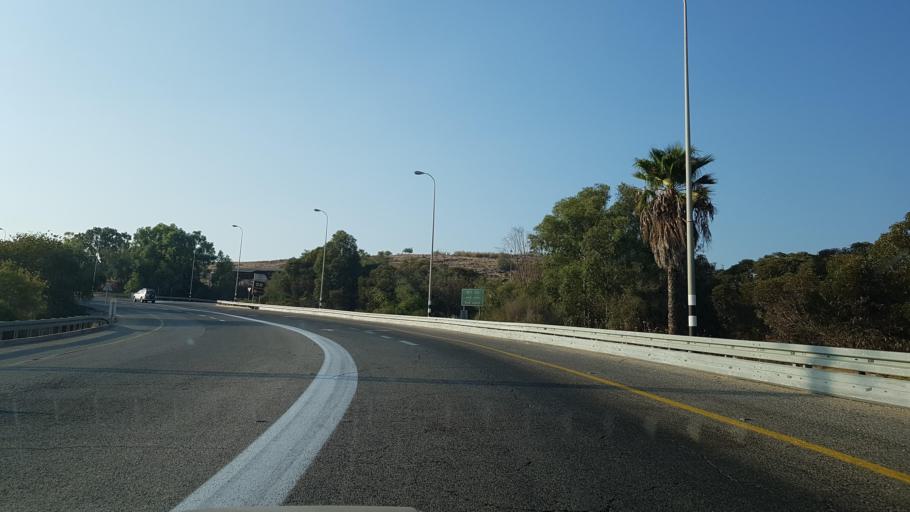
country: SY
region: Quneitra
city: Al Butayhah
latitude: 32.9118
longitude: 35.5980
